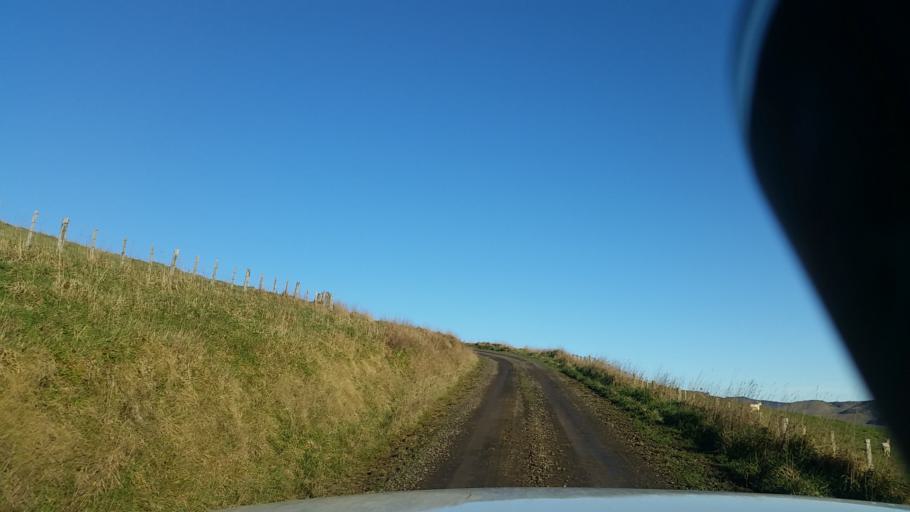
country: NZ
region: Canterbury
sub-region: Christchurch City
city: Christchurch
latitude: -43.7236
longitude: 173.0512
